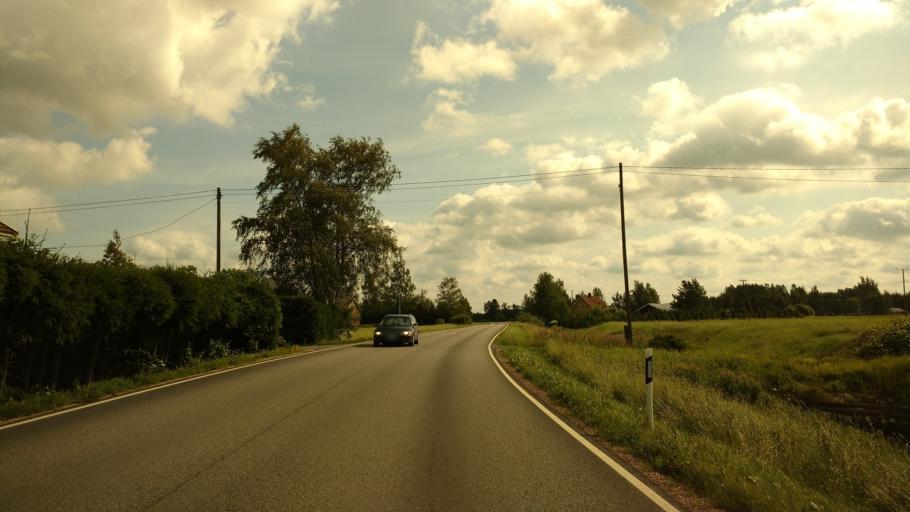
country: FI
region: Varsinais-Suomi
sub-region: Loimaa
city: Koski Tl
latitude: 60.6429
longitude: 23.1109
